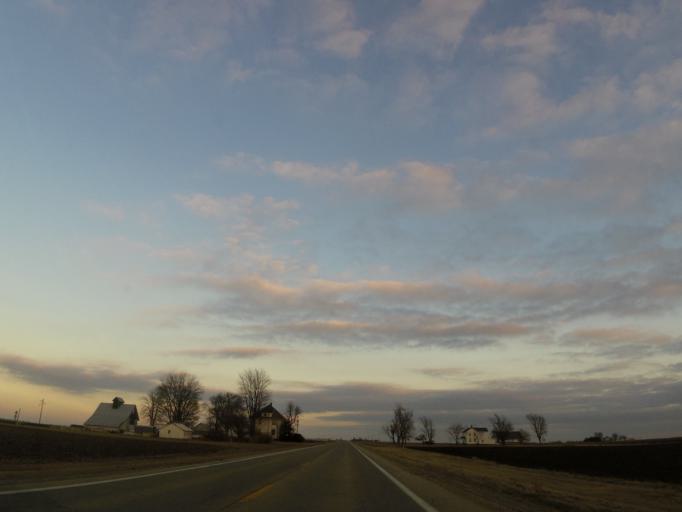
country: US
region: Illinois
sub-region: Woodford County
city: El Paso
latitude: 40.7385
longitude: -88.9524
